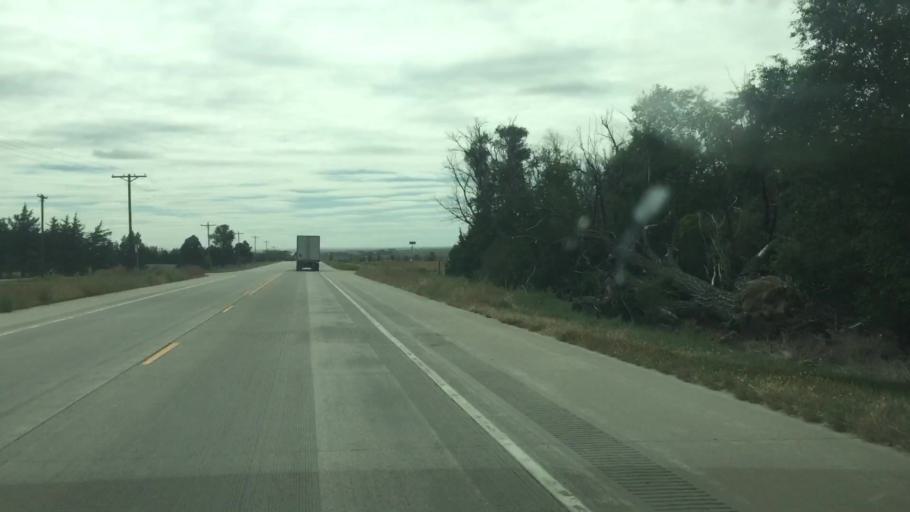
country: US
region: Colorado
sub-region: Prowers County
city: Lamar
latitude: 38.1877
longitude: -102.7243
